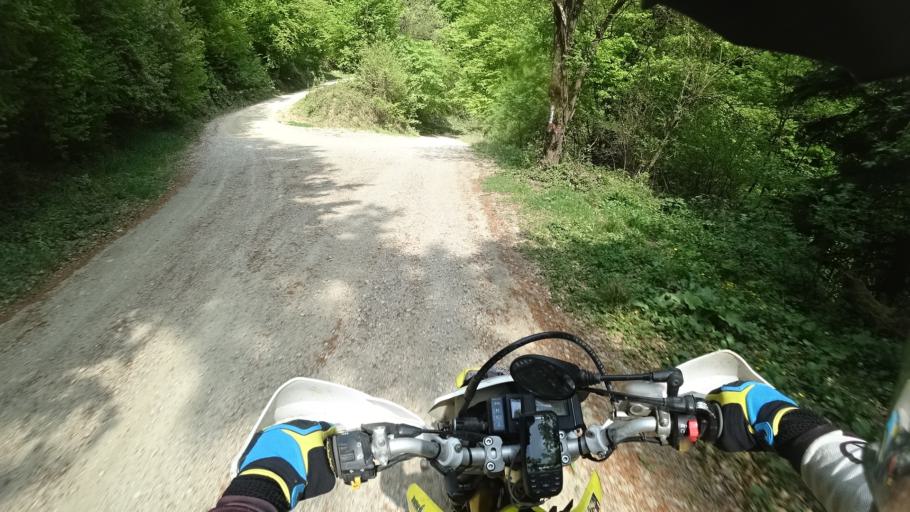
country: HR
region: Grad Zagreb
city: Kasina
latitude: 45.9246
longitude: 16.0229
